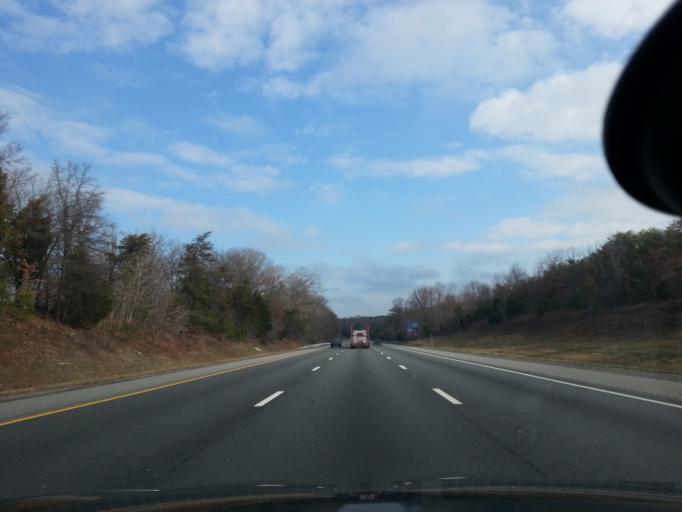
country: US
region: Virginia
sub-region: Spotsylvania County
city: Spotsylvania Courthouse
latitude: 38.2024
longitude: -77.4989
